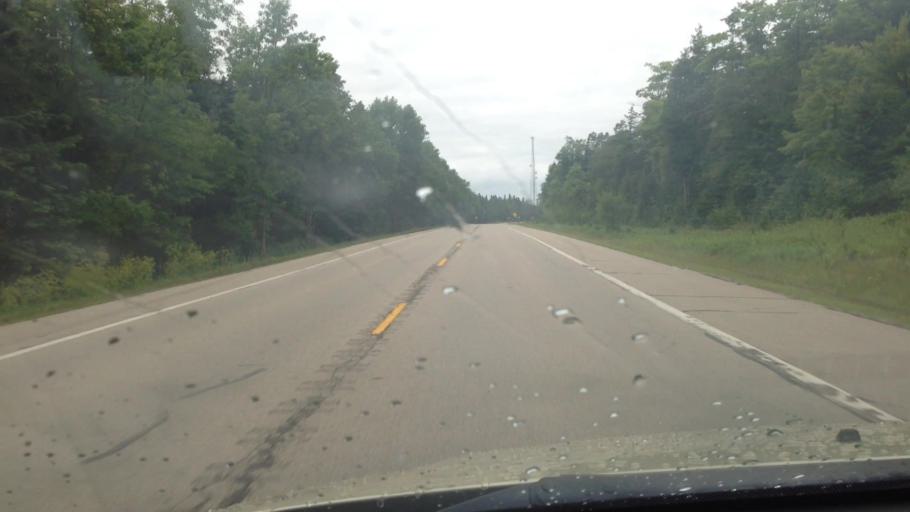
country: US
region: Michigan
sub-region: Menominee County
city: Menominee
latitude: 45.4019
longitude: -87.3634
